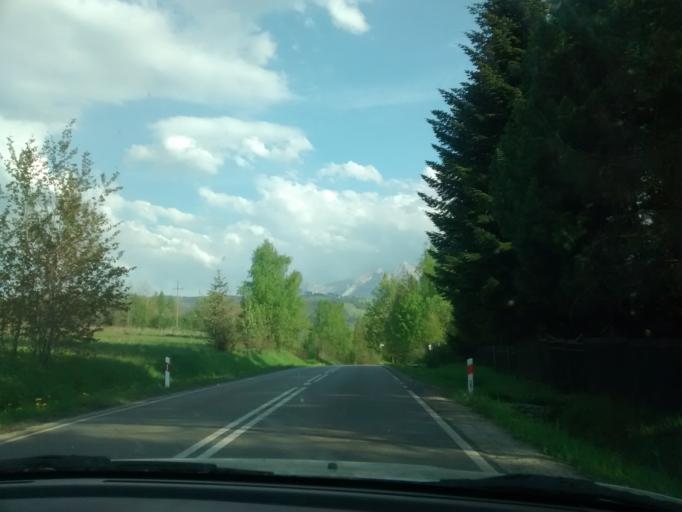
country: PL
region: Lesser Poland Voivodeship
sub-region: Powiat tatrzanski
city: Bukowina Tatrzanska
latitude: 49.3375
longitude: 20.1449
